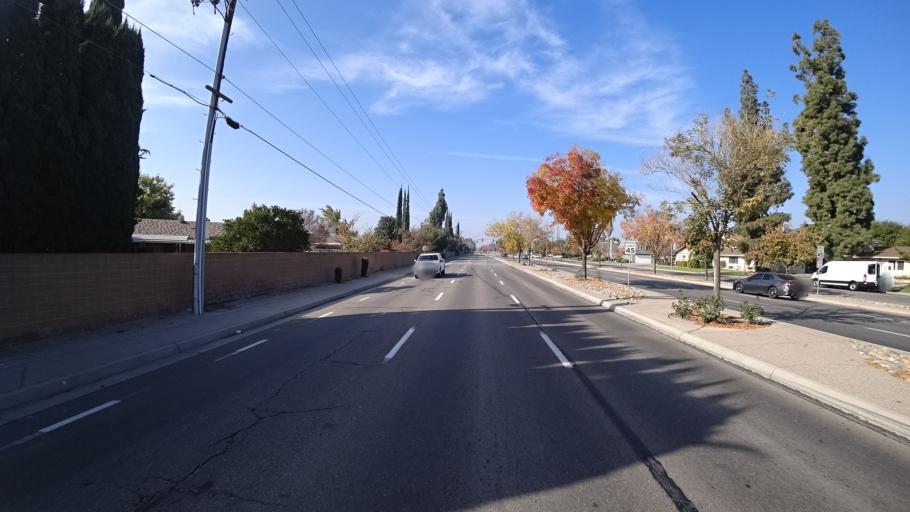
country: US
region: California
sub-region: Kern County
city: Greenacres
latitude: 35.3542
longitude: -119.0675
